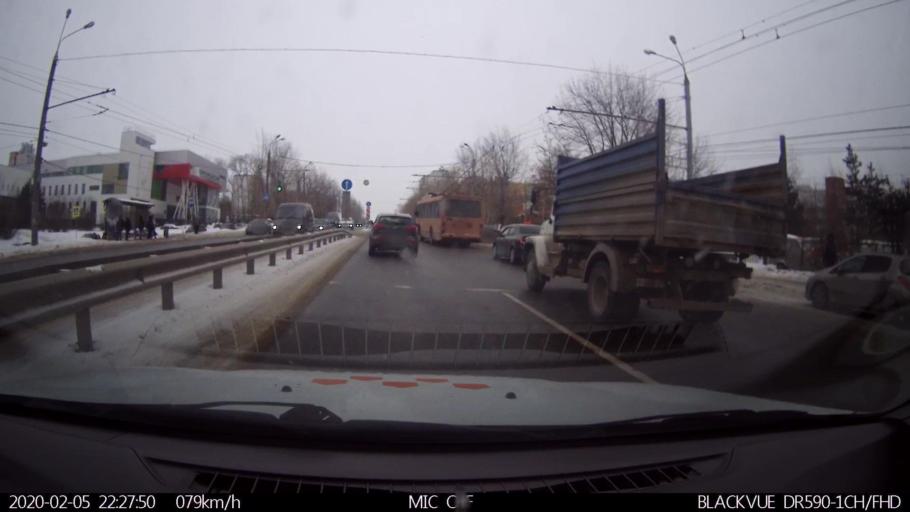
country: RU
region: Nizjnij Novgorod
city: Imeni Stepana Razina
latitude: 54.7610
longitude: 44.1203
